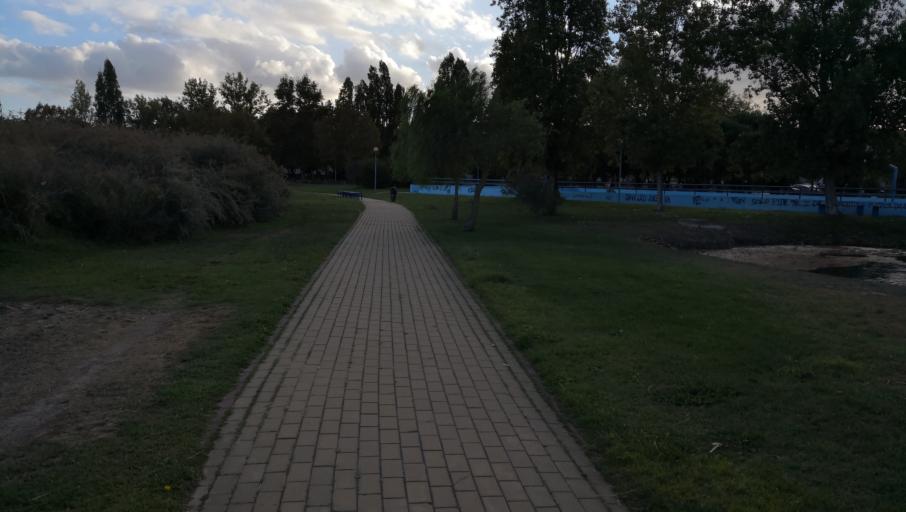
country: PT
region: Setubal
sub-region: Moita
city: Alhos Vedros
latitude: 38.6655
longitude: -9.0429
